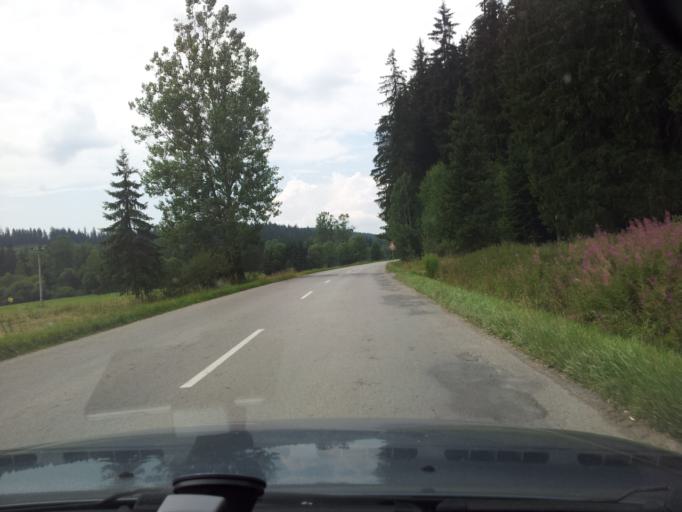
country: SK
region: Zilinsky
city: Oravska Lesna
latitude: 49.3765
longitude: 19.2630
